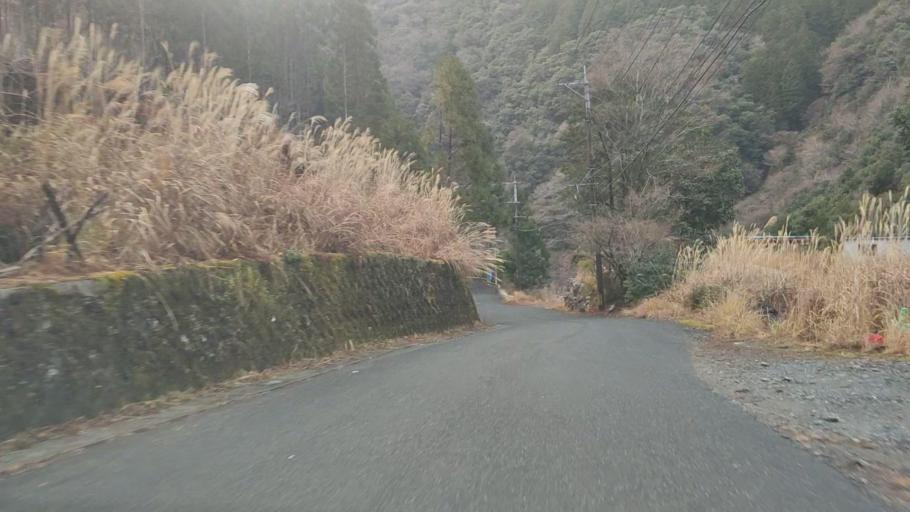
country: JP
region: Kumamoto
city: Matsubase
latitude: 32.4856
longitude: 130.8968
